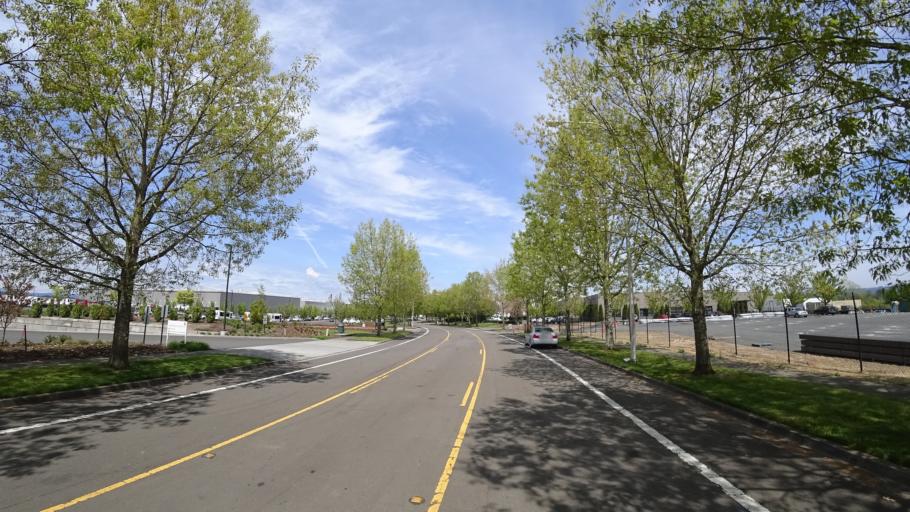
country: US
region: Oregon
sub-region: Washington County
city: Rockcreek
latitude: 45.5679
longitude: -122.9101
